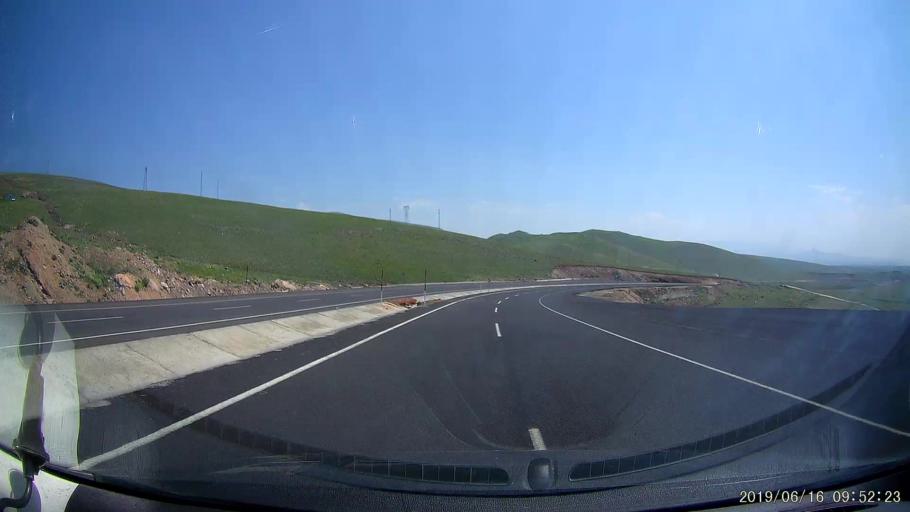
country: TR
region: Kars
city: Digor
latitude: 40.3937
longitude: 43.3857
